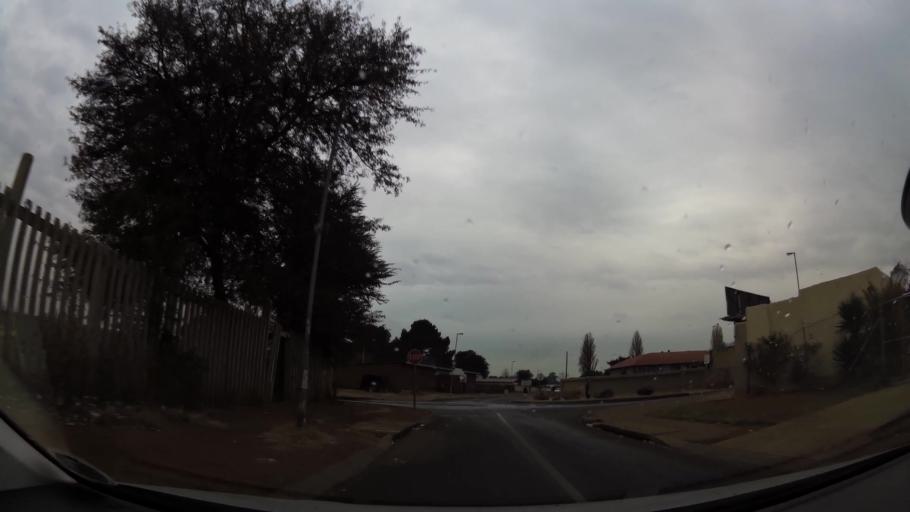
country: ZA
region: Gauteng
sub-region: City of Johannesburg Metropolitan Municipality
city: Soweto
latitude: -26.2476
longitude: 27.8763
